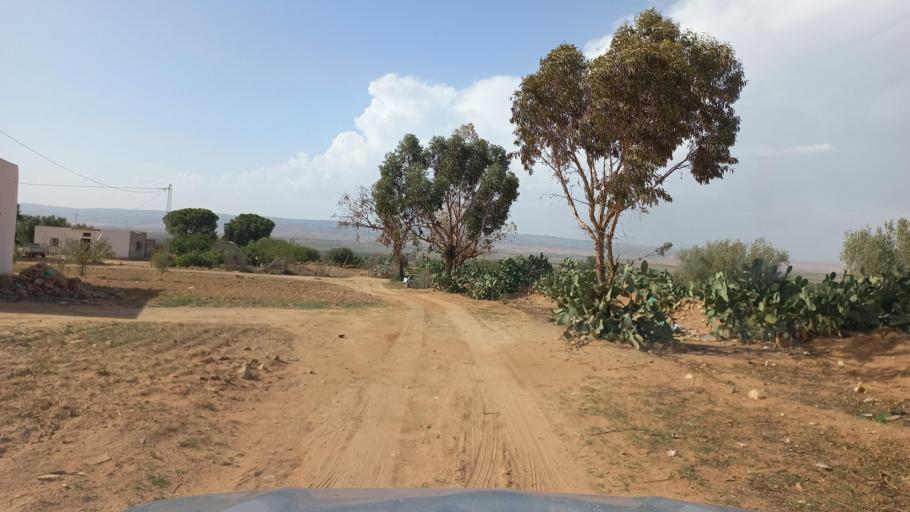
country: TN
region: Al Qasrayn
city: Kasserine
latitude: 35.2057
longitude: 8.9694
